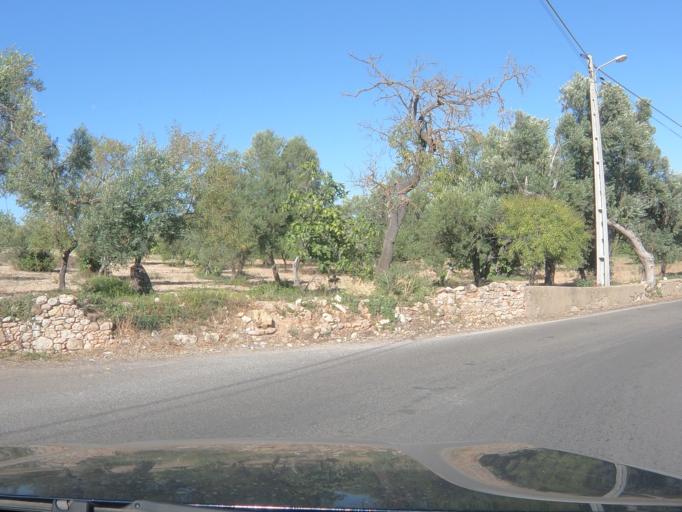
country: PT
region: Faro
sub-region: Loule
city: Loule
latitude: 37.1171
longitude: -8.0228
